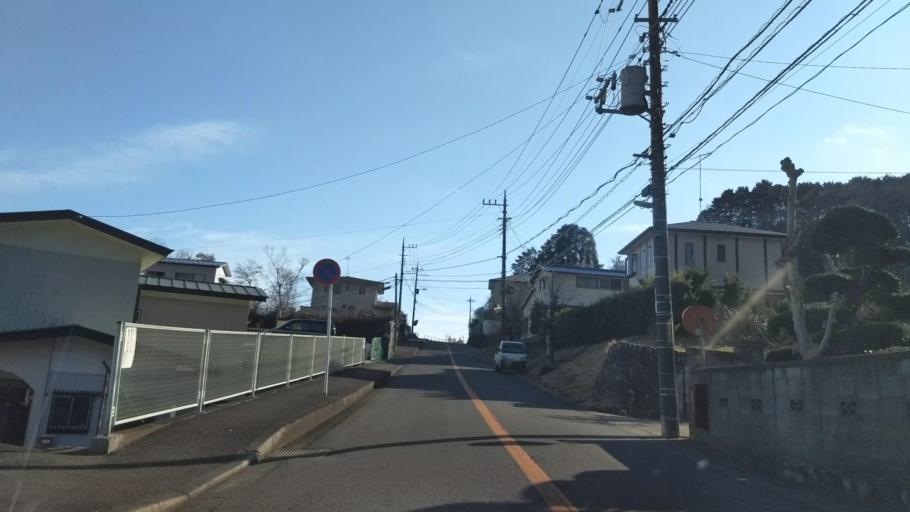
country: JP
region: Kanagawa
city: Hadano
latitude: 35.3691
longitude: 139.2518
